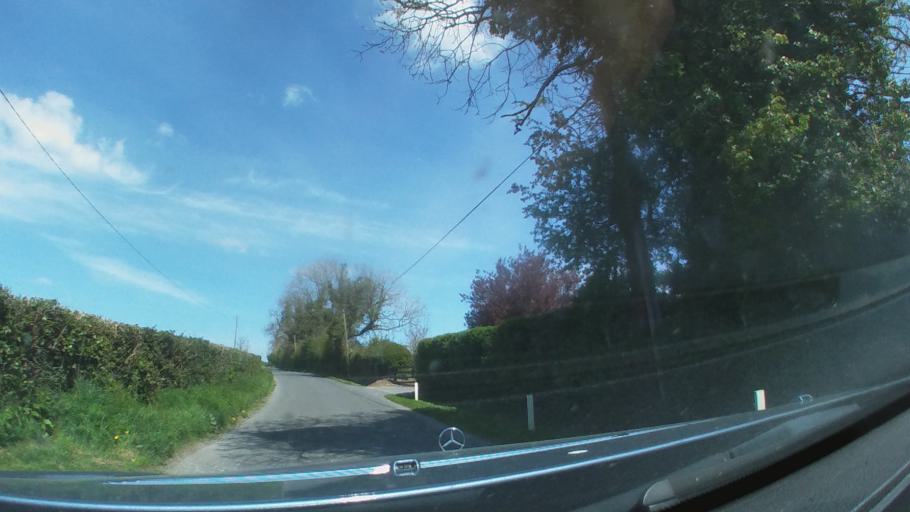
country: IE
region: Leinster
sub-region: Kilkenny
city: Callan
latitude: 52.6022
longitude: -7.3930
